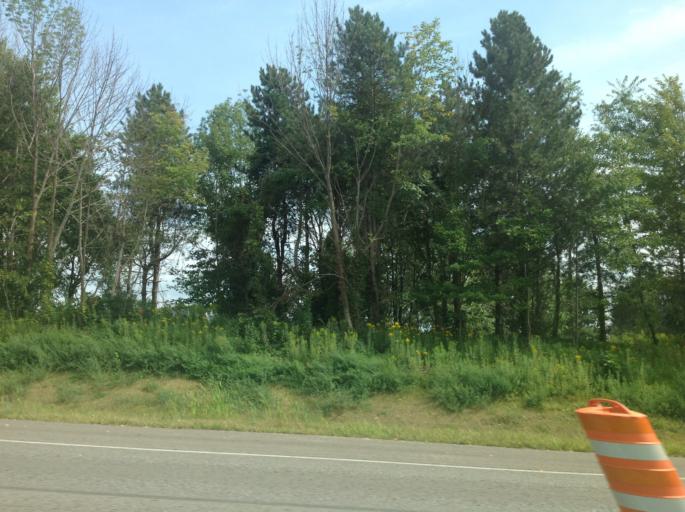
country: US
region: Ohio
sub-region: Morrow County
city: Cardington
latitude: 40.4388
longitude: -82.8065
